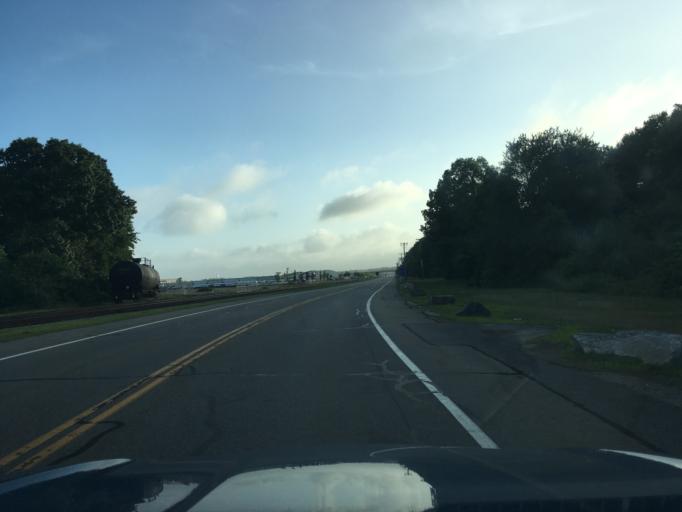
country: US
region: Rhode Island
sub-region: Kent County
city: East Greenwich
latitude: 41.6120
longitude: -71.4283
